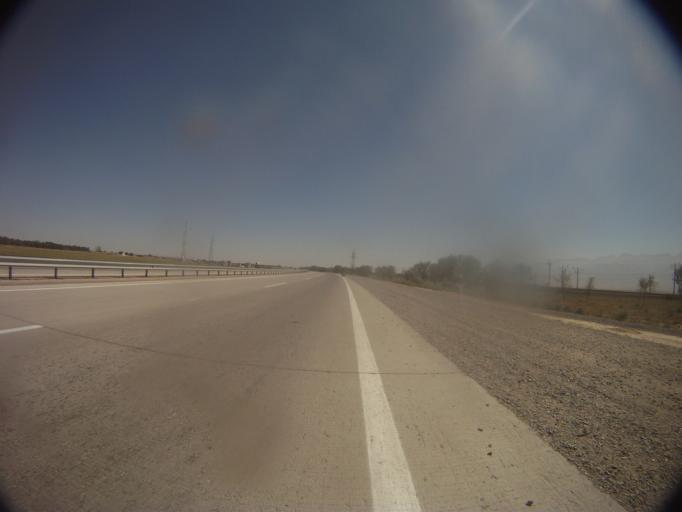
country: KG
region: Talas
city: Ivanovo-Alekseyevka
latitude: 42.9898
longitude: 72.1177
